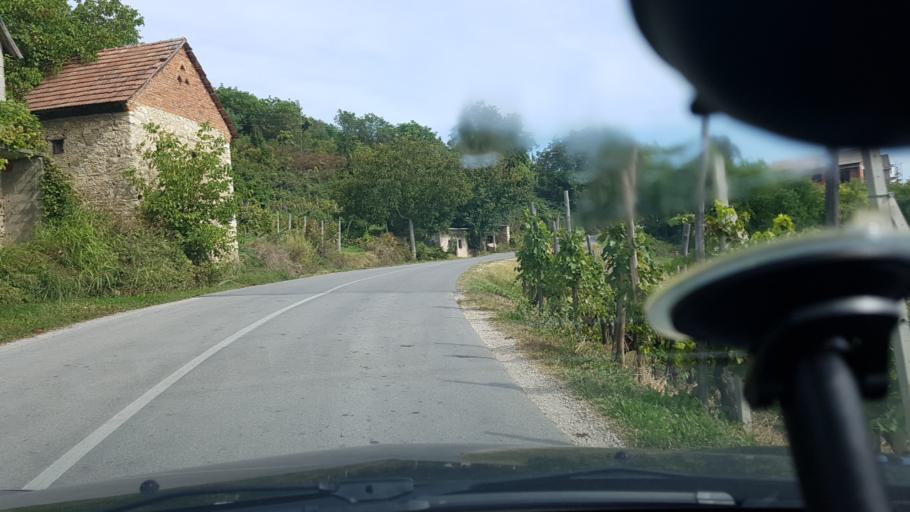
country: HR
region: Varazdinska
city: Ljubescica
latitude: 46.0954
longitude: 16.3355
